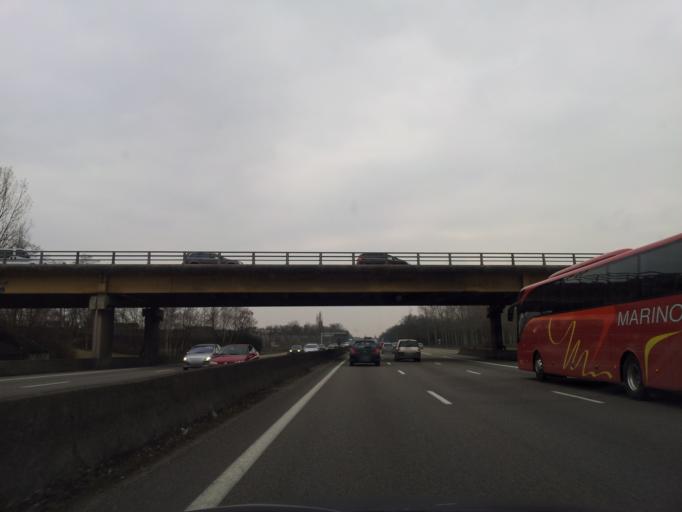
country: FR
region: Alsace
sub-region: Departement du Bas-Rhin
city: Ostwald
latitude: 48.5466
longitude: 7.7281
